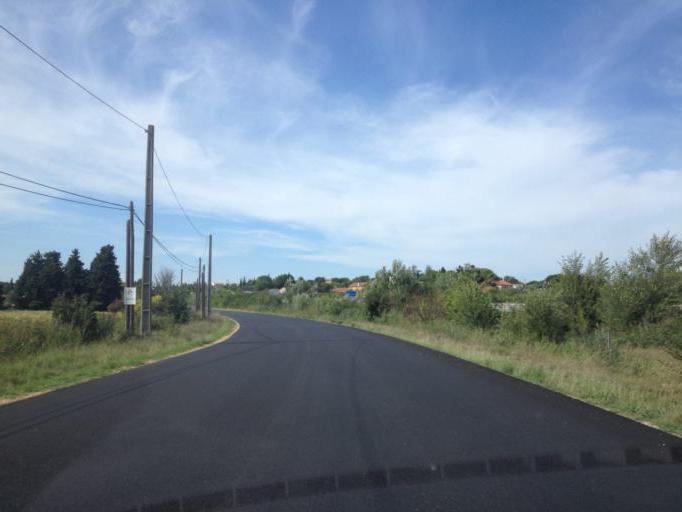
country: FR
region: Provence-Alpes-Cote d'Azur
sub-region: Departement du Vaucluse
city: Courthezon
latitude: 44.0890
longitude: 4.8764
